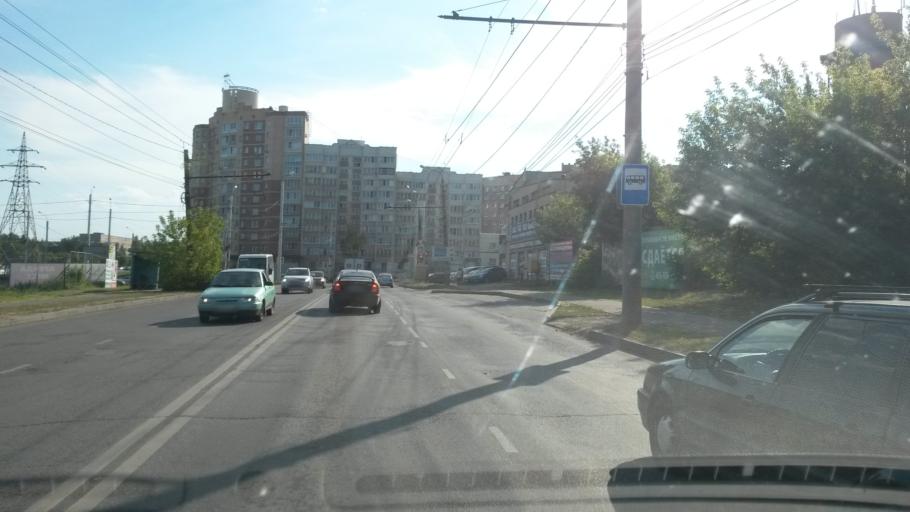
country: RU
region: Ivanovo
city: Kokhma
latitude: 56.9620
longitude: 41.0304
